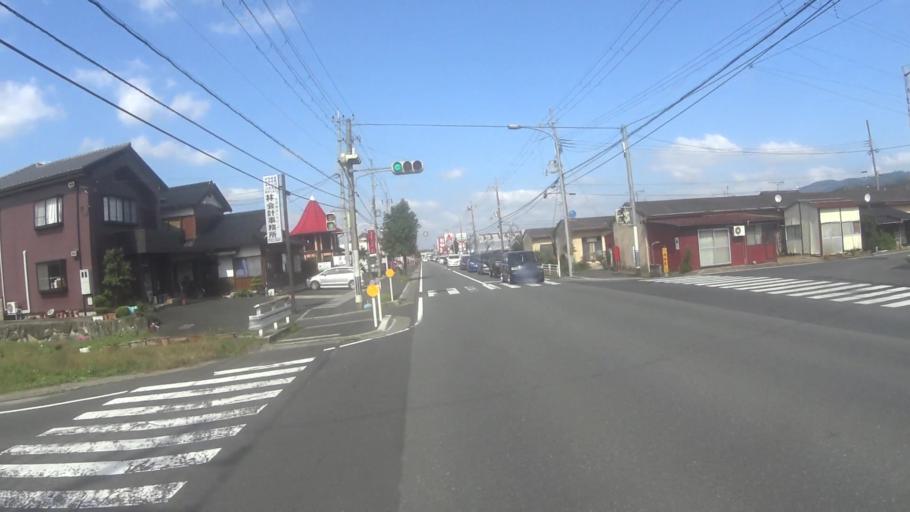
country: JP
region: Kyoto
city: Miyazu
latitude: 35.5887
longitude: 135.0955
